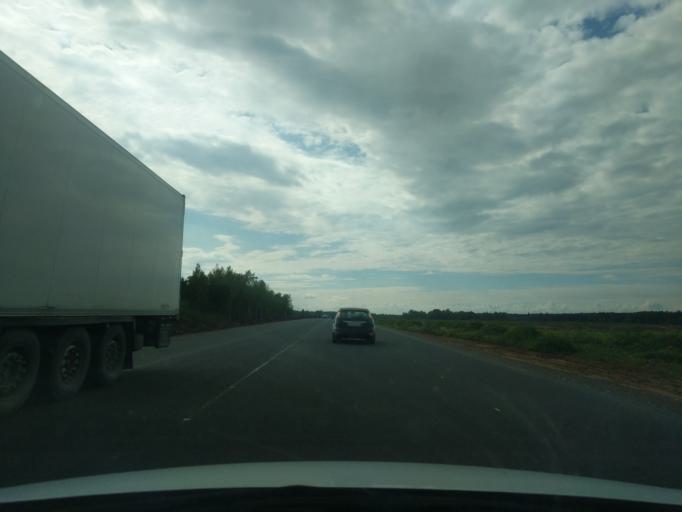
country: RU
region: Kostroma
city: Sudislavl'
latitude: 57.8323
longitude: 41.5472
